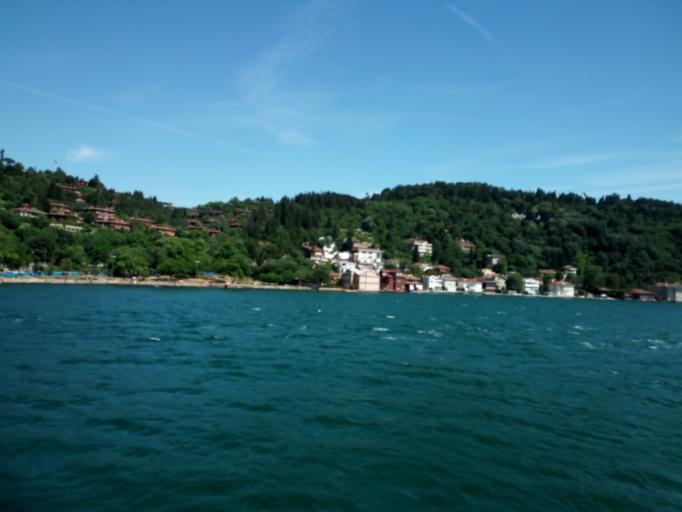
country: TR
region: Istanbul
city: UEskuedar
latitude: 41.0693
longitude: 29.0542
